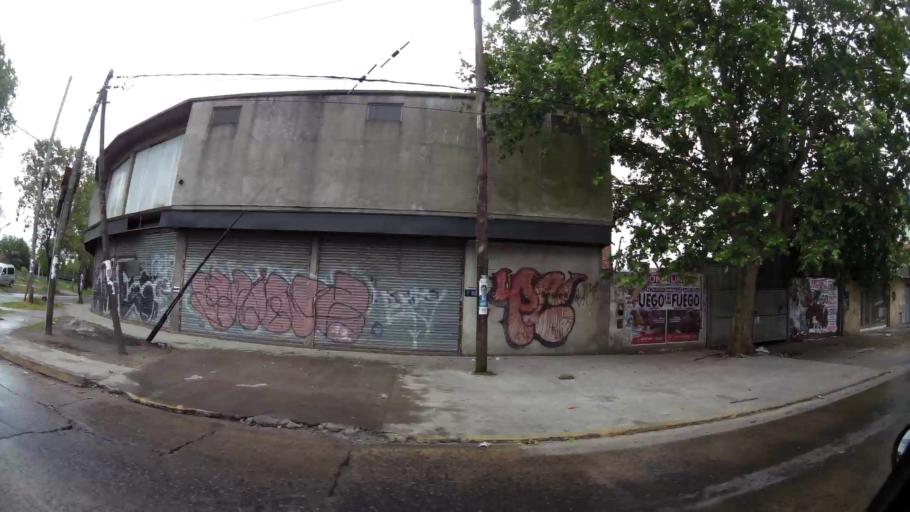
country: AR
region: Buenos Aires
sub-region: Partido de Quilmes
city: Quilmes
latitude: -34.7536
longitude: -58.2297
